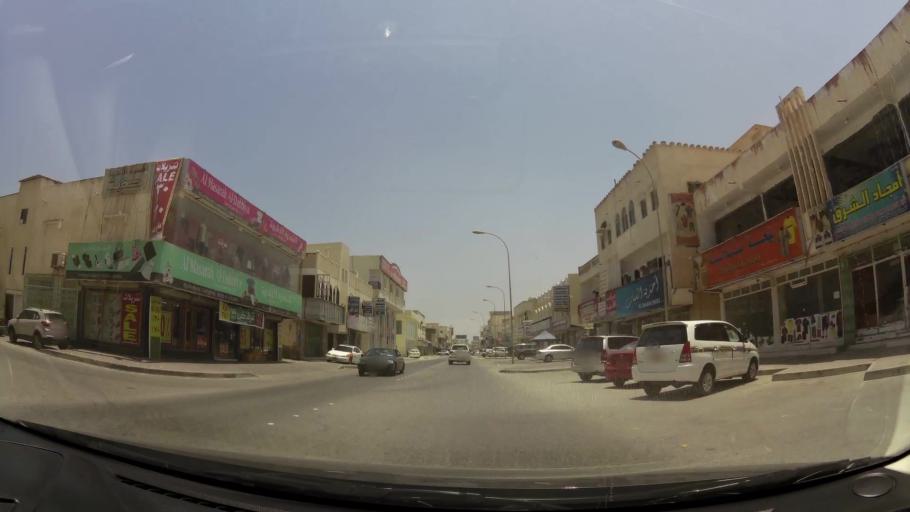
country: OM
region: Zufar
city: Salalah
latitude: 17.0139
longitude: 54.1023
